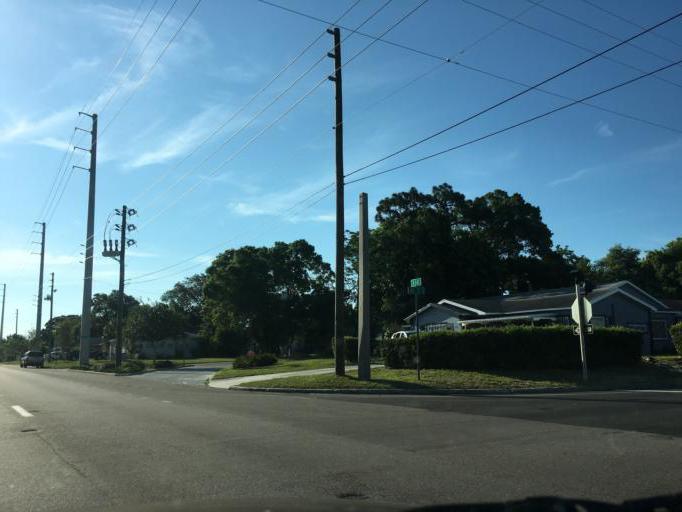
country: US
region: Florida
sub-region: Pinellas County
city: Saint Petersburg
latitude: 27.7701
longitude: -82.6878
